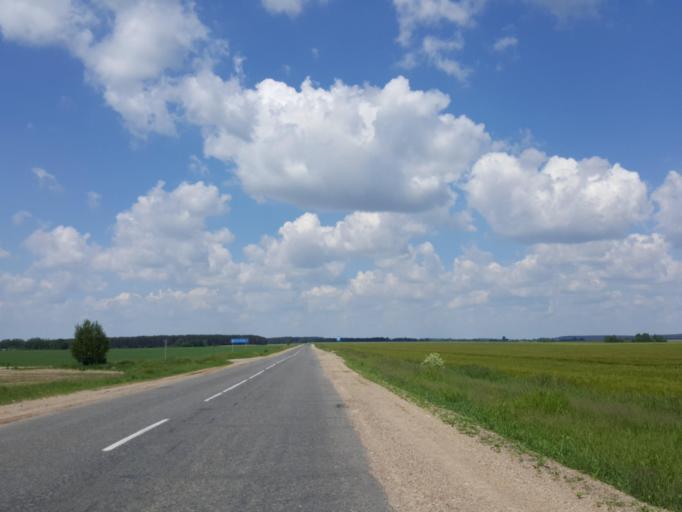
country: BY
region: Brest
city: Kamyanyets
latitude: 52.4030
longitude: 23.7682
